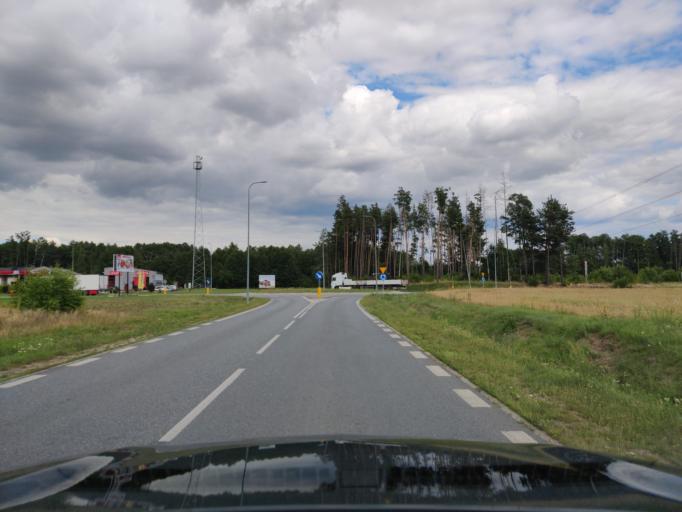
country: PL
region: Masovian Voivodeship
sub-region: Powiat sokolowski
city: Kosow Lacki
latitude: 52.5830
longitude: 22.1527
